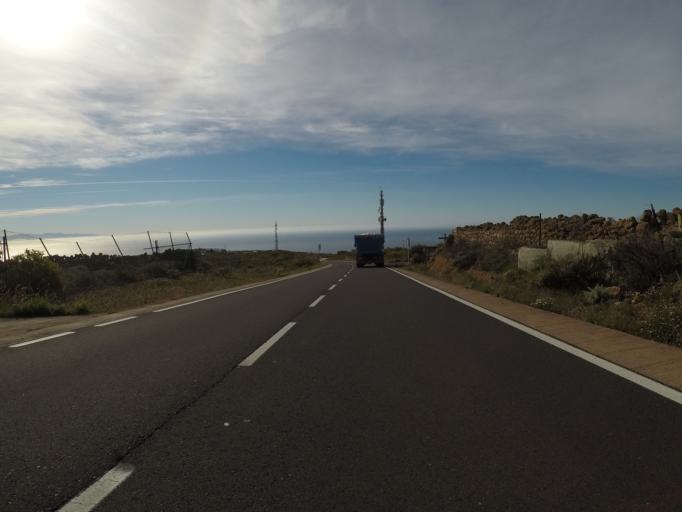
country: ES
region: Canary Islands
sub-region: Provincia de Santa Cruz de Tenerife
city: Lomo de Arico
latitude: 28.1634
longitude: -16.4979
